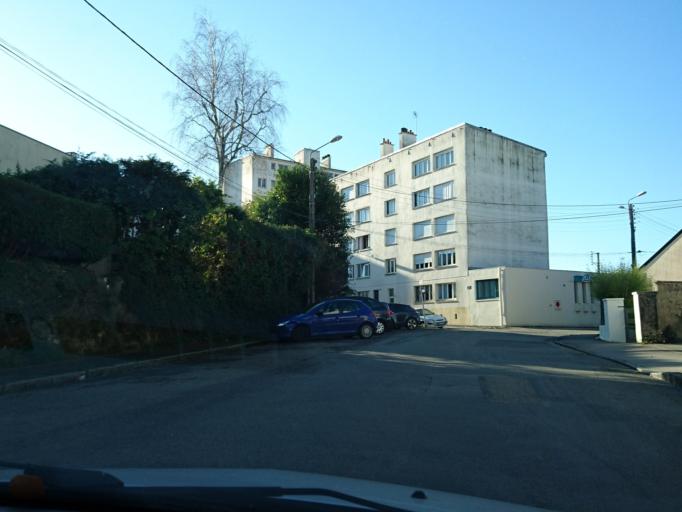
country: FR
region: Brittany
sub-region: Departement du Finistere
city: Brest
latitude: 48.4101
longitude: -4.4543
